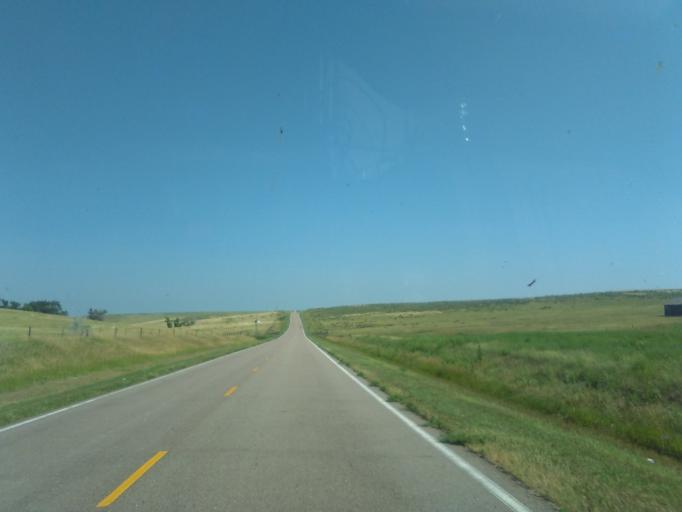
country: US
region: Nebraska
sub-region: Dundy County
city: Benkelman
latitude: 39.9324
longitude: -101.5413
